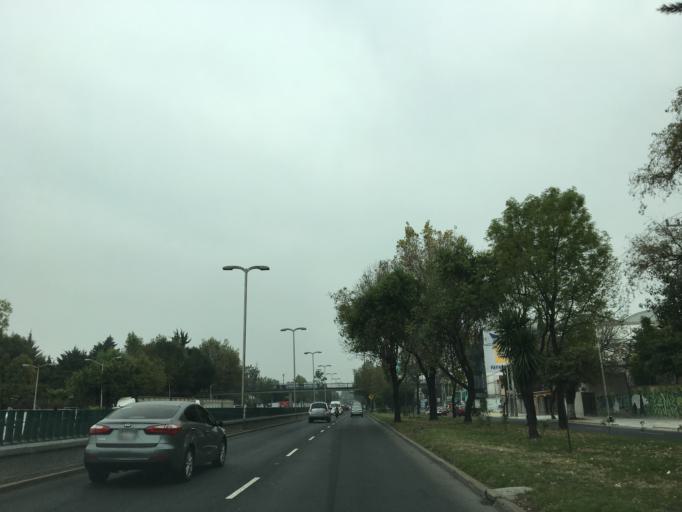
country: MX
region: Mexico City
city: Tlalpan
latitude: 19.3027
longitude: -99.1437
